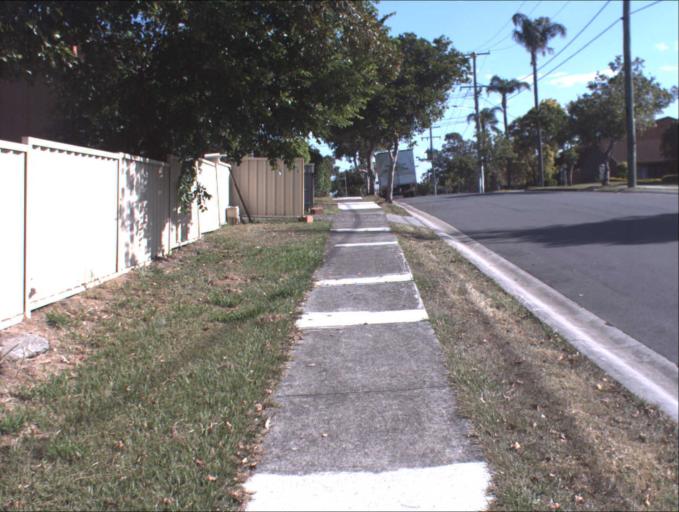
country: AU
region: Queensland
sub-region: Logan
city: Rochedale South
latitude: -27.5996
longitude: 153.1169
